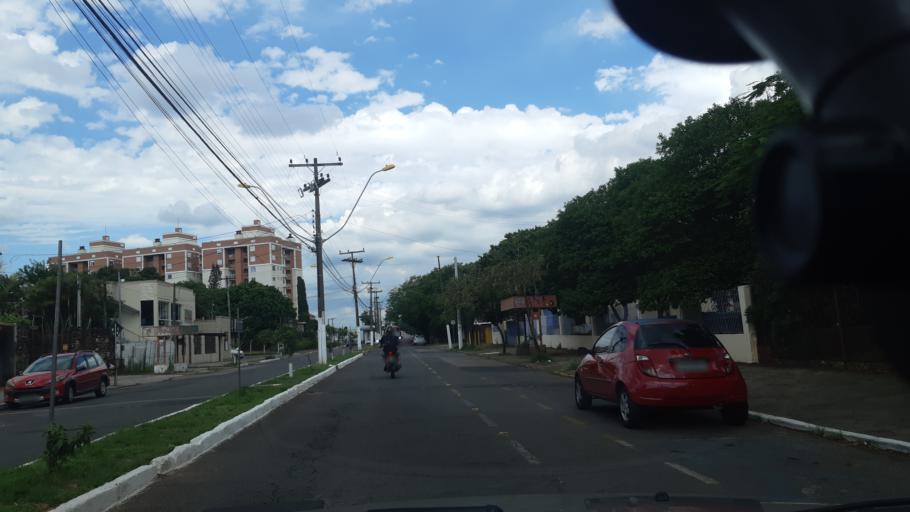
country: BR
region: Rio Grande do Sul
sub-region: Sapucaia Do Sul
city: Sapucaia
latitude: -29.8493
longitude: -51.1617
